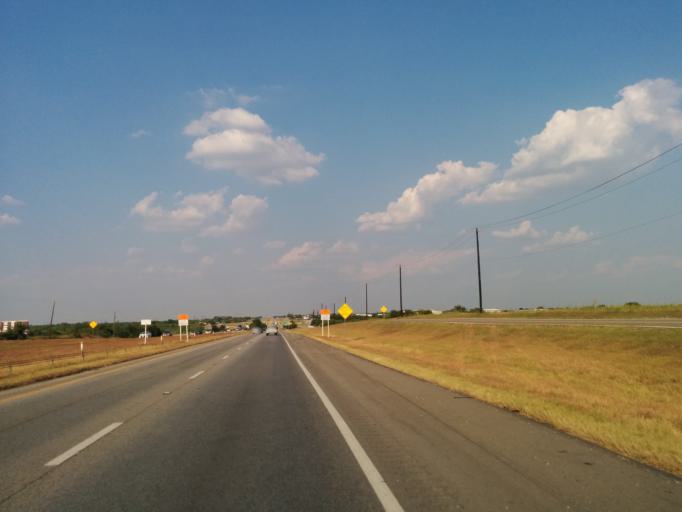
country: US
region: Texas
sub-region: Bexar County
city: Converse
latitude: 29.4702
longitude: -98.2763
